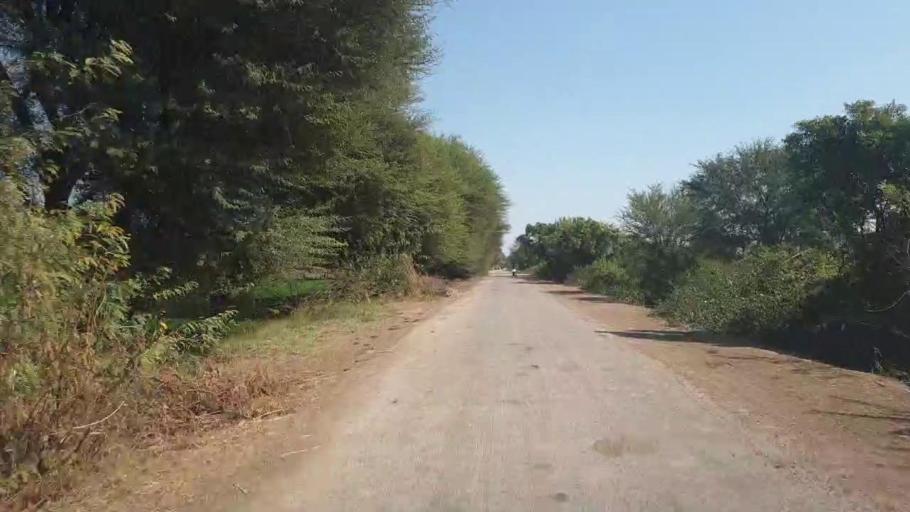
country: PK
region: Sindh
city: Chambar
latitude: 25.2887
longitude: 68.6844
